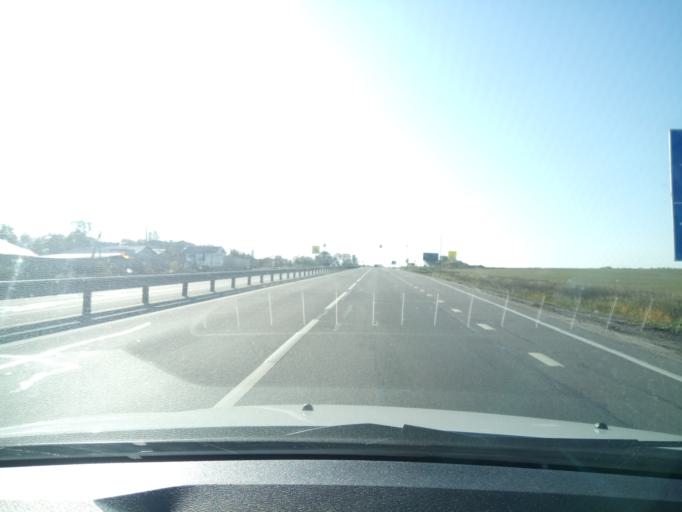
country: RU
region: Nizjnij Novgorod
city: Burevestnik
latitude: 56.1469
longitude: 43.9100
